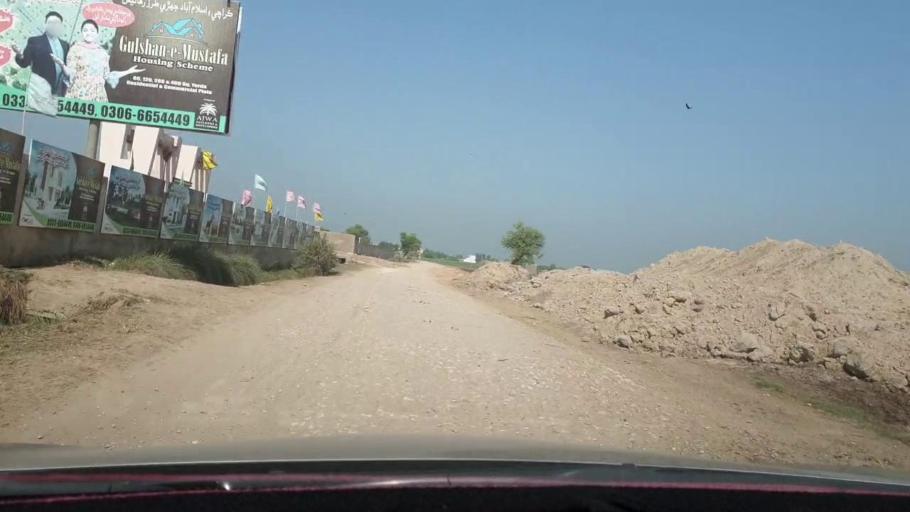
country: PK
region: Sindh
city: Kambar
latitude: 27.5979
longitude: 67.9854
